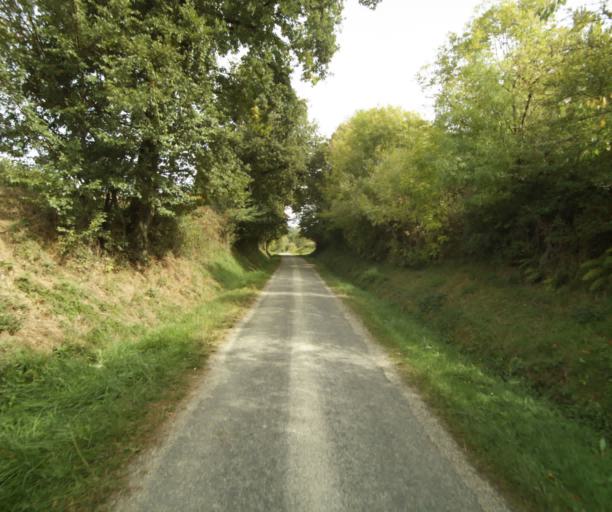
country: FR
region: Midi-Pyrenees
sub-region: Departement du Gers
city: Eauze
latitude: 43.8353
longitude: 0.1299
